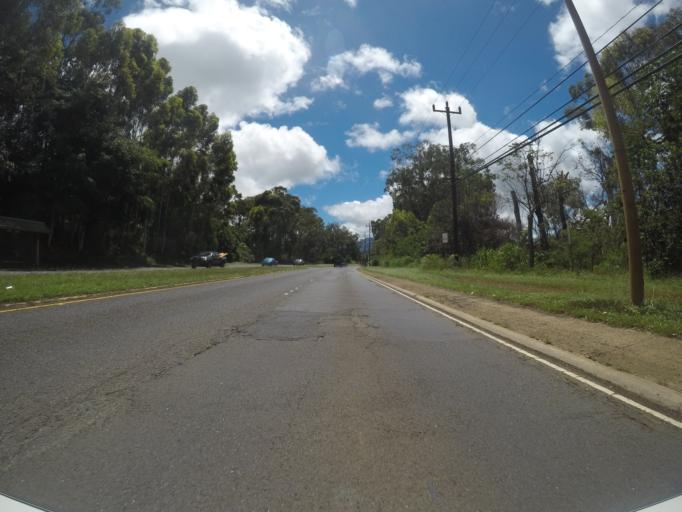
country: US
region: Hawaii
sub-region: Honolulu County
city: Wahiawa
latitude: 21.4888
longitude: -158.0410
